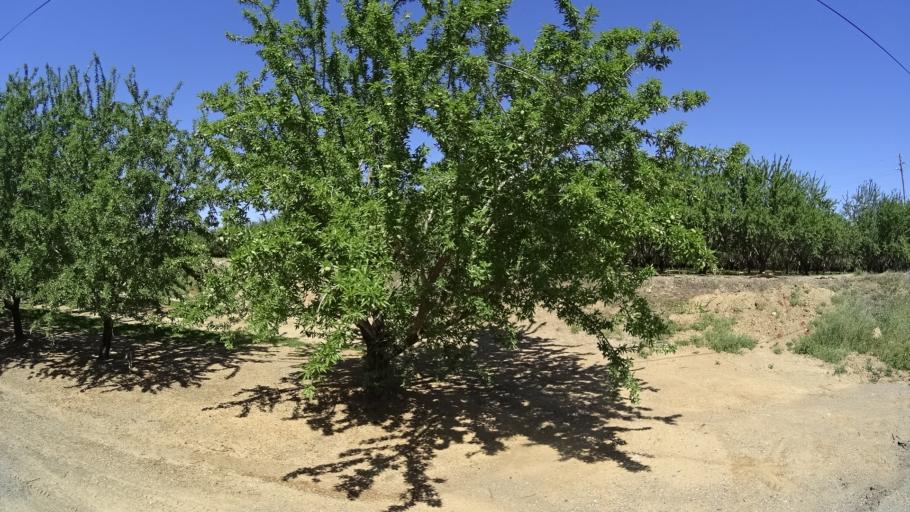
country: US
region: California
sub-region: Glenn County
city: Hamilton City
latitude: 39.7323
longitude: -122.0962
